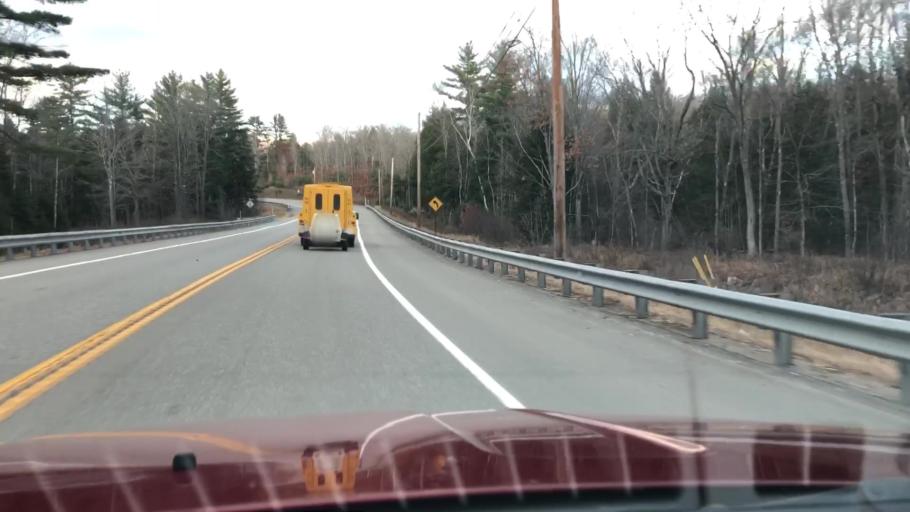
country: US
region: Maine
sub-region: Oxford County
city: Peru
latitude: 44.5356
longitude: -70.4058
